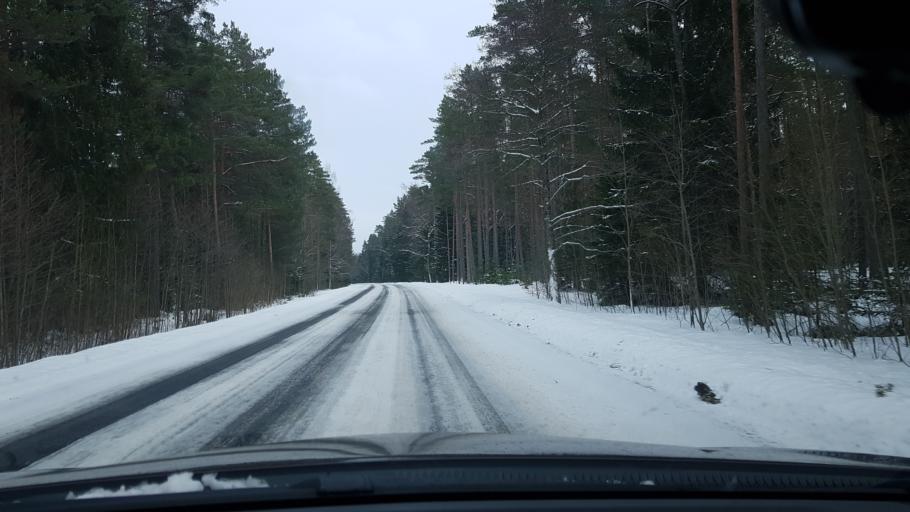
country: EE
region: Harju
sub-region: Loksa linn
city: Loksa
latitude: 59.5655
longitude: 25.8803
